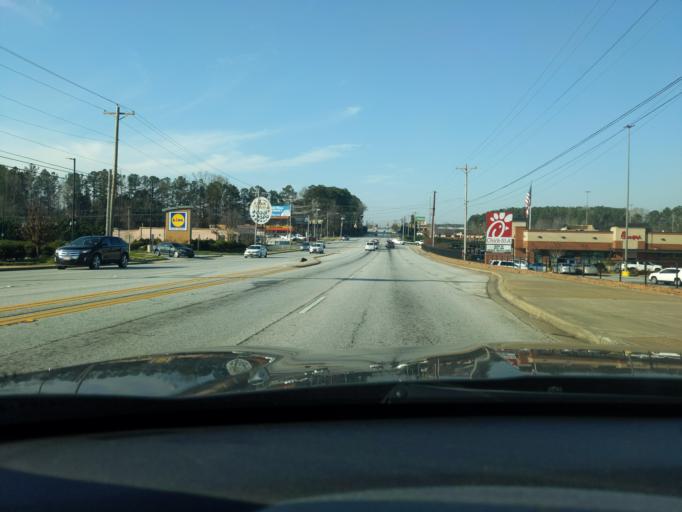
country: US
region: South Carolina
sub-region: Greenwood County
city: Greenwood
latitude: 34.2102
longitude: -82.1808
